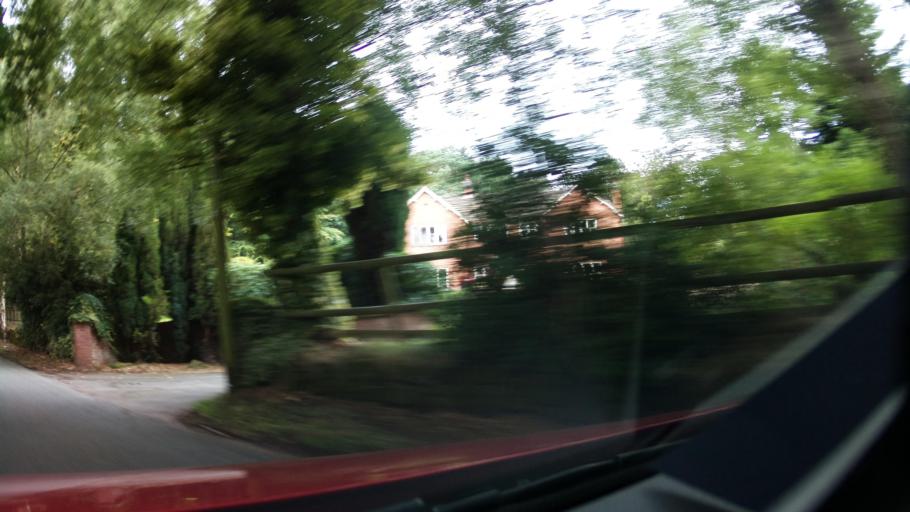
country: GB
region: England
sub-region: Staffordshire
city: Barlaston
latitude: 52.9309
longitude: -2.1976
